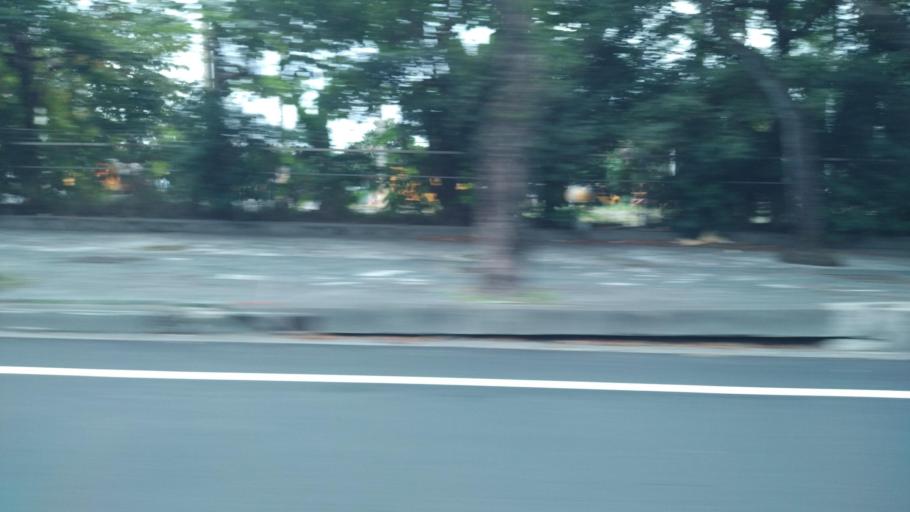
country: TW
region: Taiwan
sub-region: Hualien
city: Hualian
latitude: 24.0069
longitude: 121.6176
